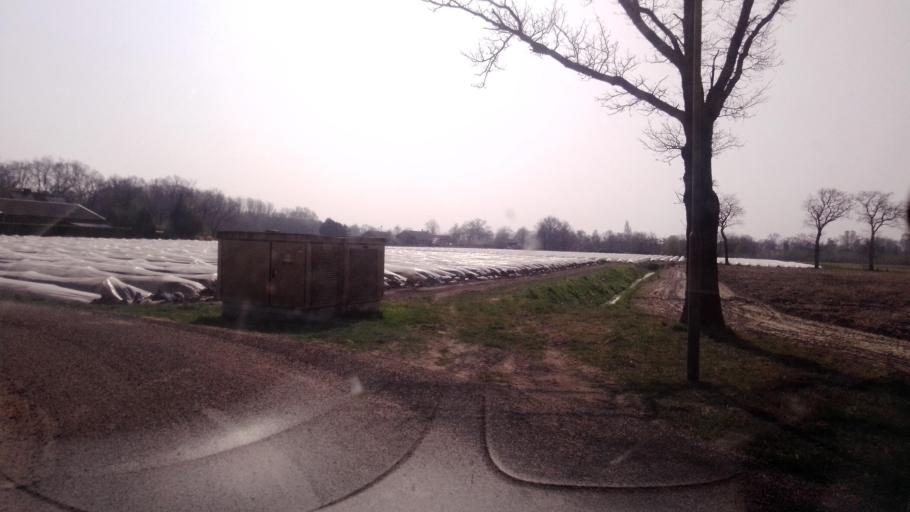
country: NL
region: Limburg
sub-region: Gemeente Peel en Maas
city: Maasbree
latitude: 51.3781
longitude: 6.0110
